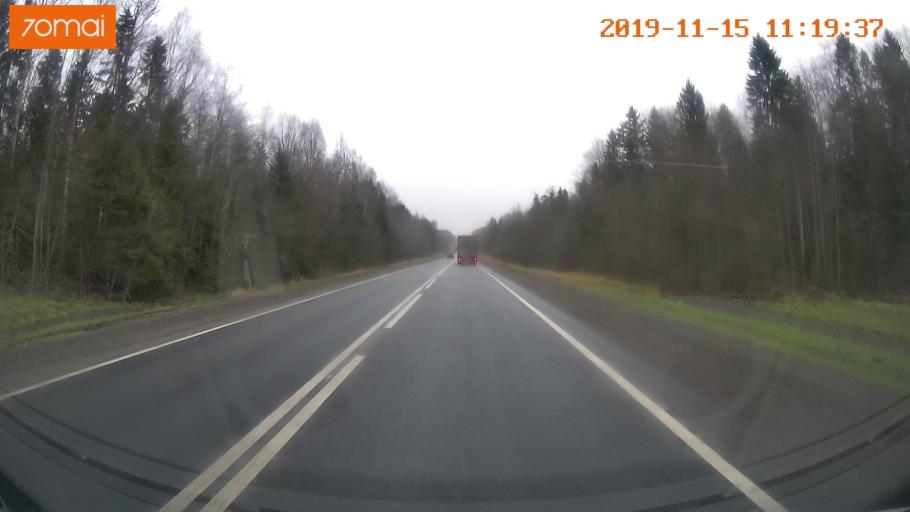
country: RU
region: Vologda
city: Molochnoye
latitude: 59.1390
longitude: 39.2958
